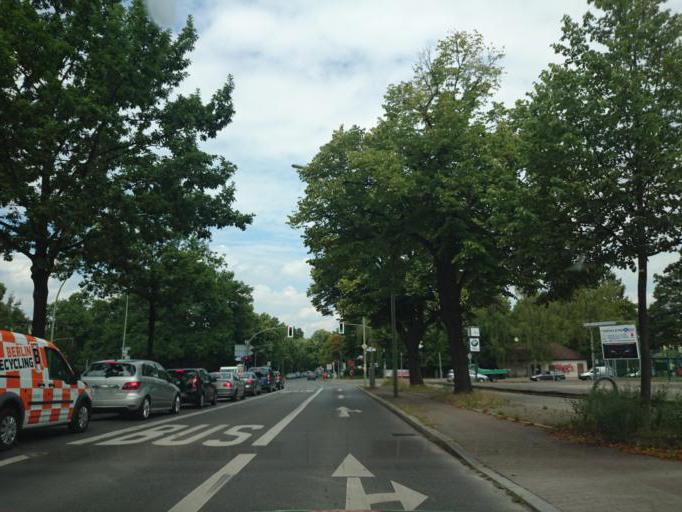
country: DE
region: Berlin
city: Lankwitz
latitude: 52.4327
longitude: 13.3534
